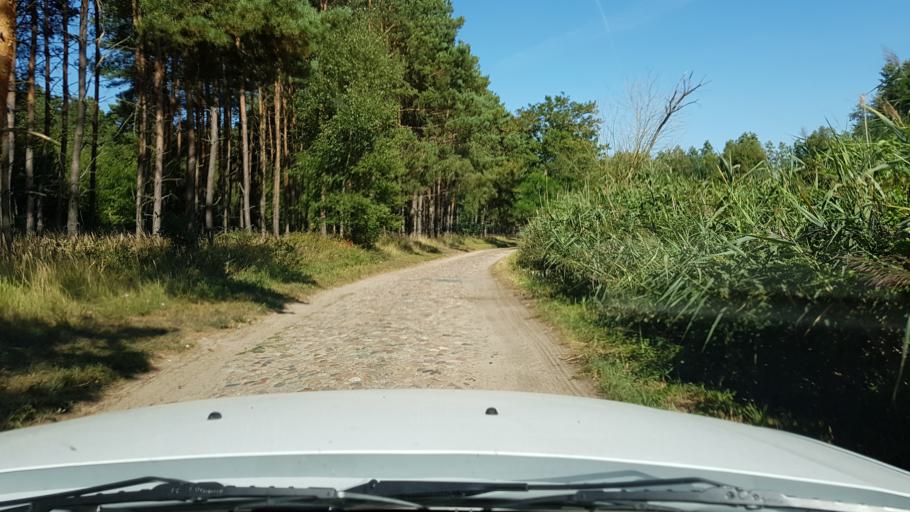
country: PL
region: West Pomeranian Voivodeship
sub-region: Powiat gryfinski
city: Cedynia
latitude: 52.8437
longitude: 14.2248
